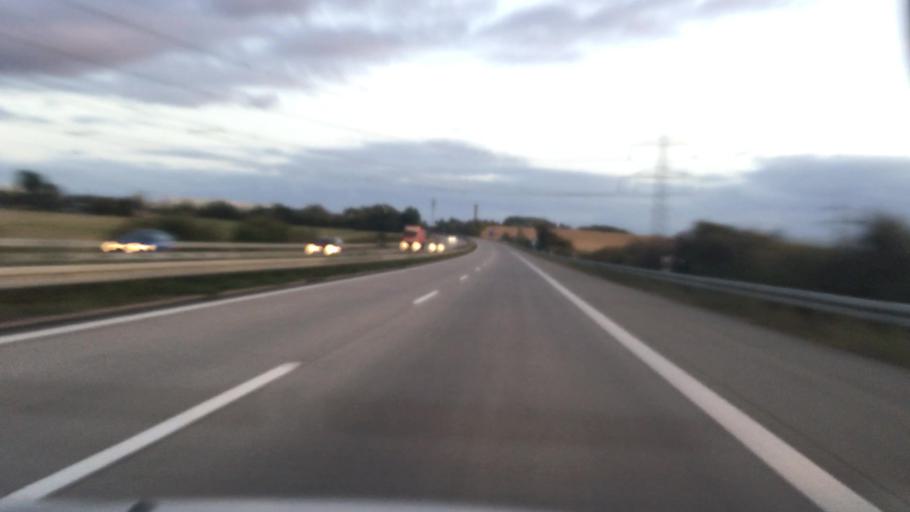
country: DE
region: Saxony
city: Mochau
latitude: 51.1199
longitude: 13.1716
